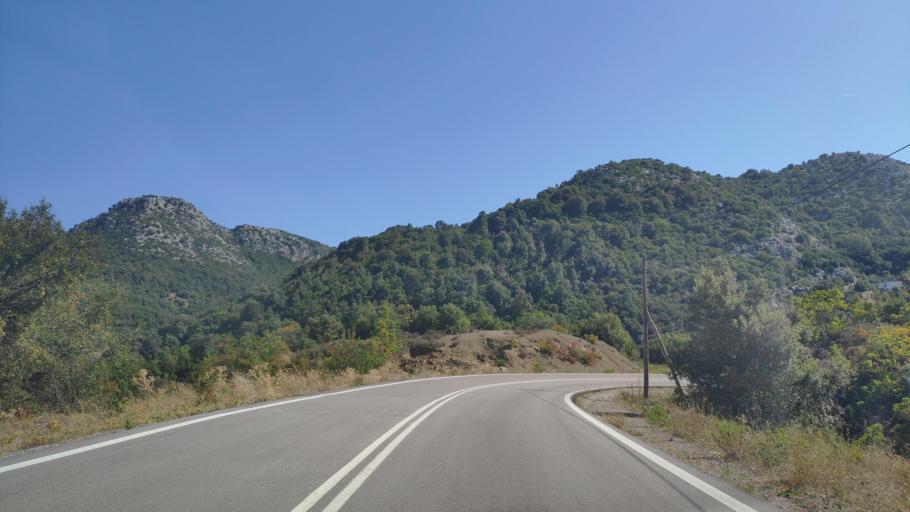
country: GR
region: West Greece
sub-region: Nomos Aitolias kai Akarnanias
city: Sardinia
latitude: 38.9254
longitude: 21.4147
